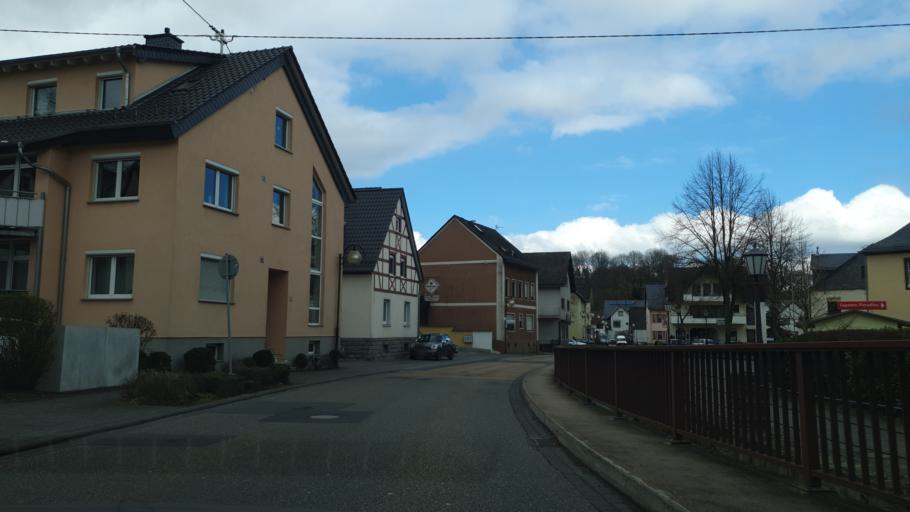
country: DE
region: Rheinland-Pfalz
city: Niederelbert
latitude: 50.4082
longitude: 7.8119
